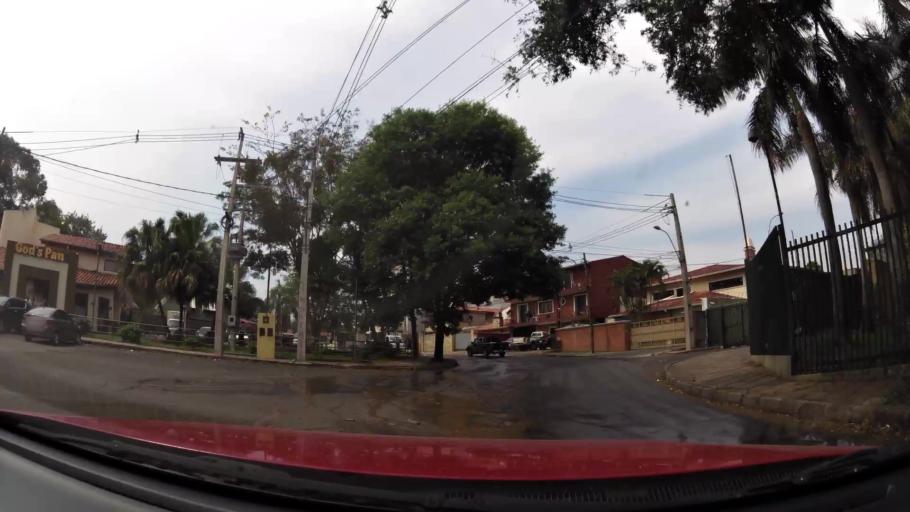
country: PY
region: Asuncion
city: Asuncion
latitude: -25.2757
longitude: -57.5769
